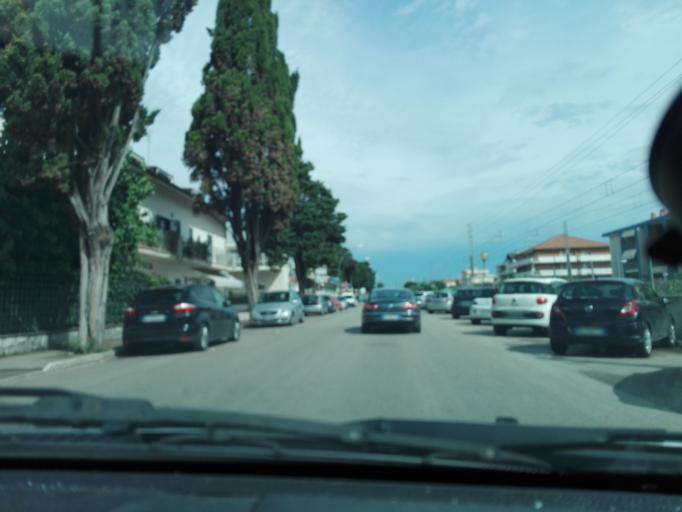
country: IT
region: Abruzzo
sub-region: Provincia di Teramo
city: Pineto
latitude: 42.6146
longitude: 14.0624
